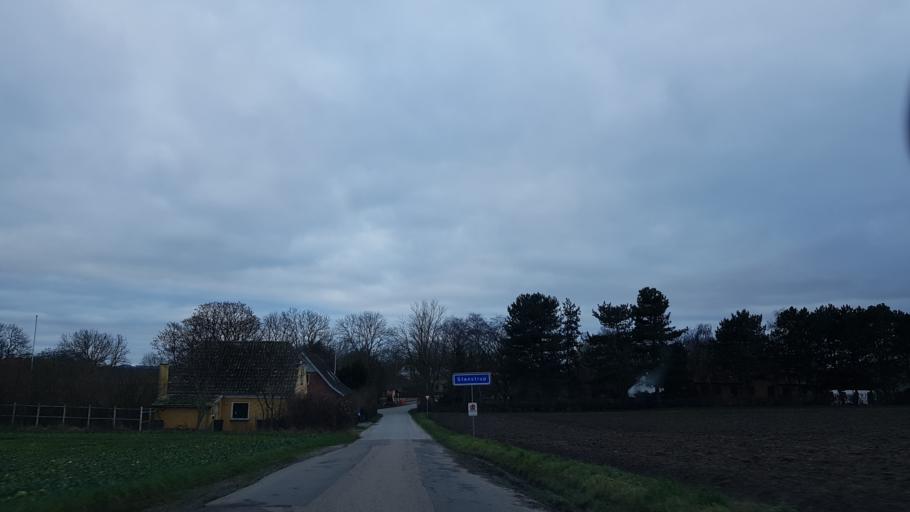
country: DK
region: Zealand
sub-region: Odsherred Kommune
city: Hojby
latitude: 55.9284
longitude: 11.5571
